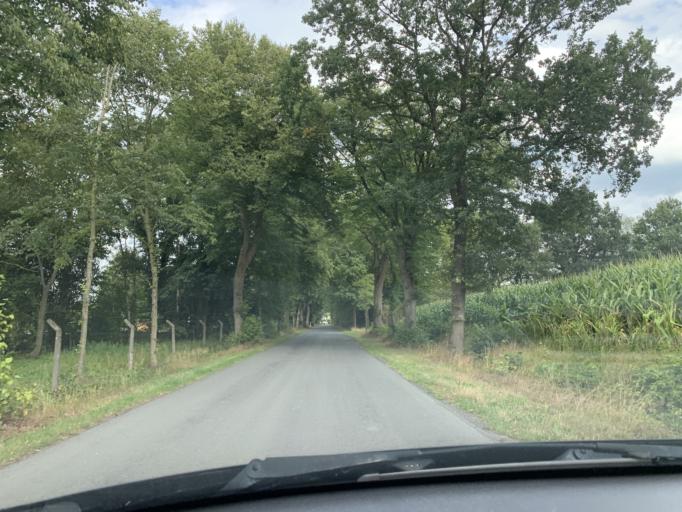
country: DE
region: Lower Saxony
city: Westerstede
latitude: 53.2548
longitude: 7.8634
